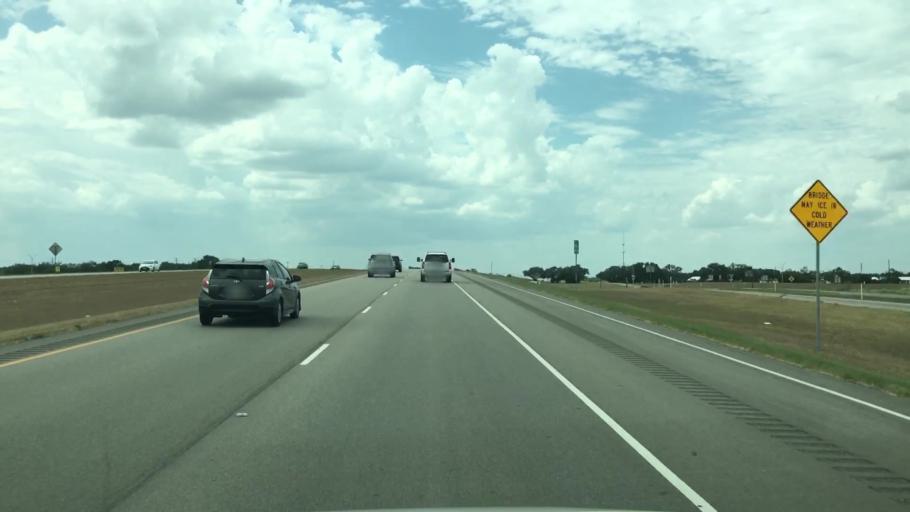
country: US
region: Texas
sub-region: Live Oak County
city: Three Rivers
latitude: 28.4872
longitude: -98.1398
